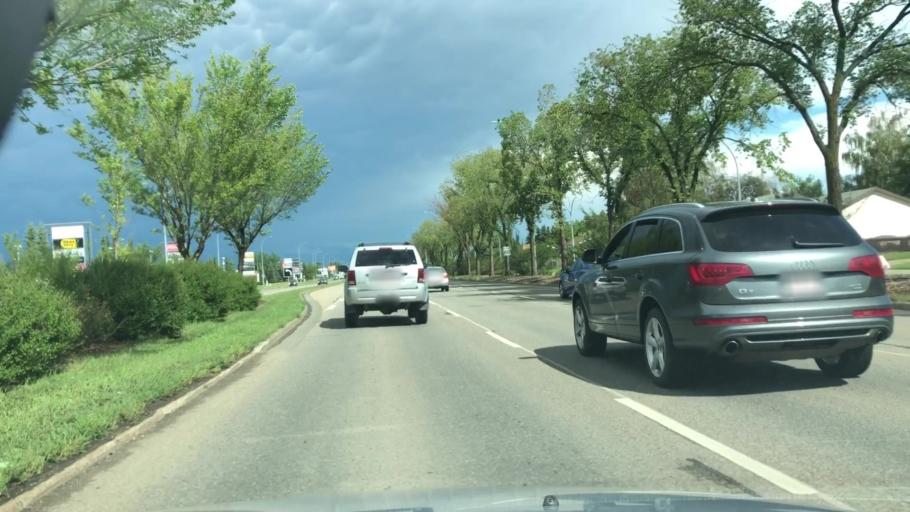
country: CA
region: Alberta
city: St. Albert
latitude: 53.5994
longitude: -113.5618
